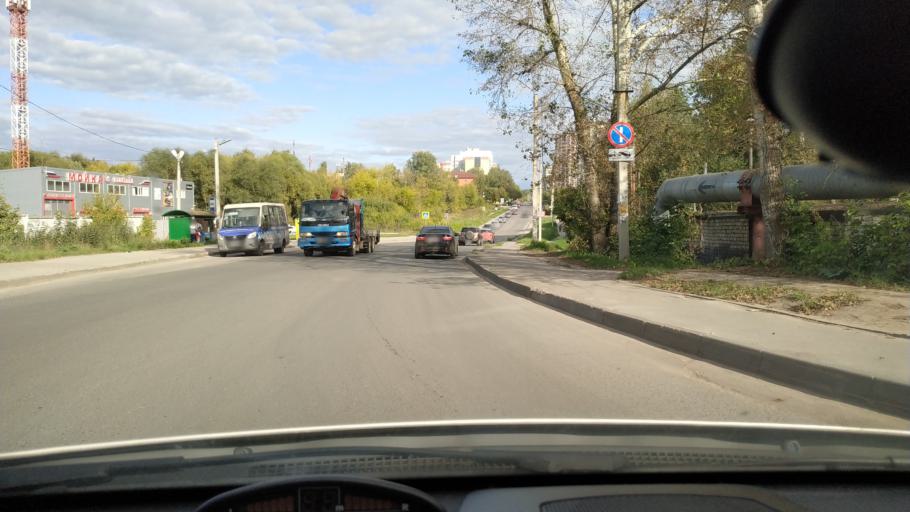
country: RU
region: Rjazan
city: Ryazan'
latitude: 54.6062
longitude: 39.7304
